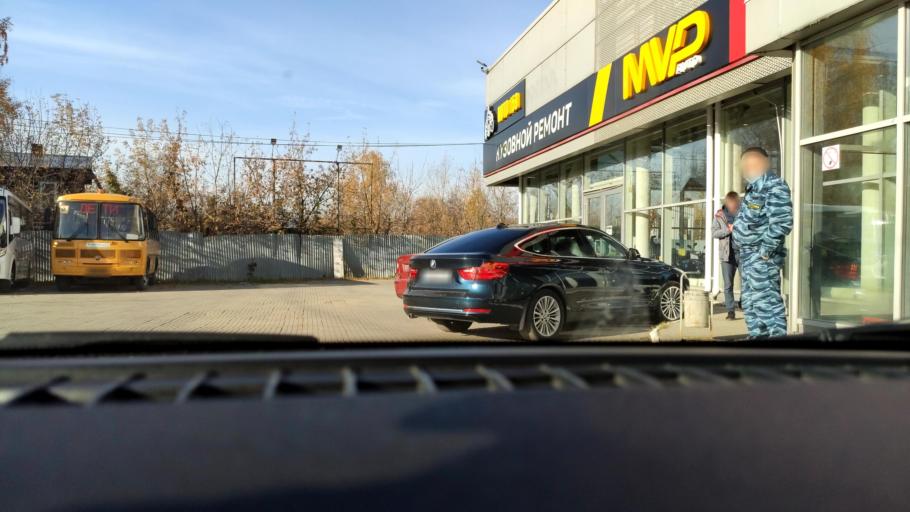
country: RU
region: Perm
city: Perm
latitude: 58.0392
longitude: 56.3153
